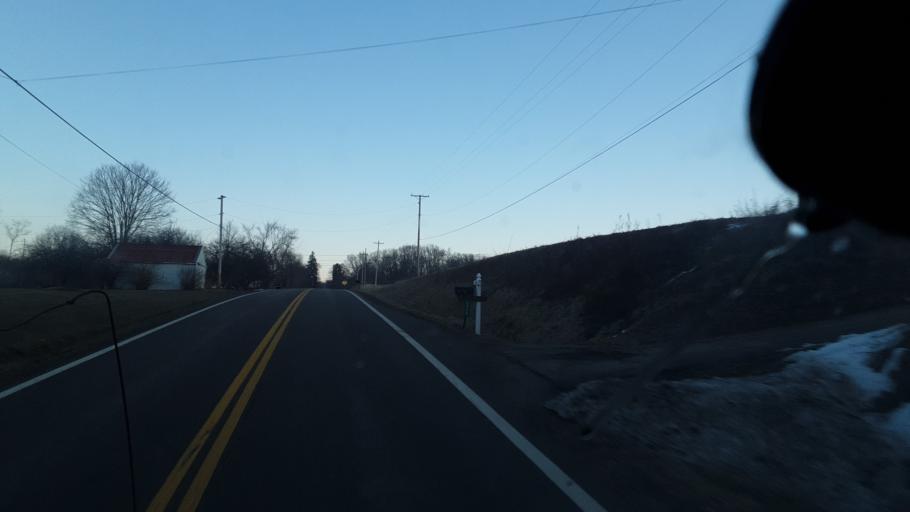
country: US
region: Ohio
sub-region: Perry County
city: Somerset
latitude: 39.7951
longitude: -82.3007
